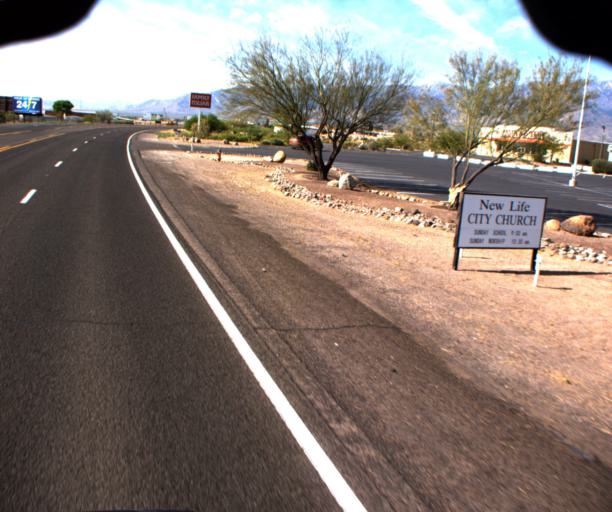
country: US
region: Arizona
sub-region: Graham County
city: Cactus Flat
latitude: 32.7922
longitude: -109.7080
